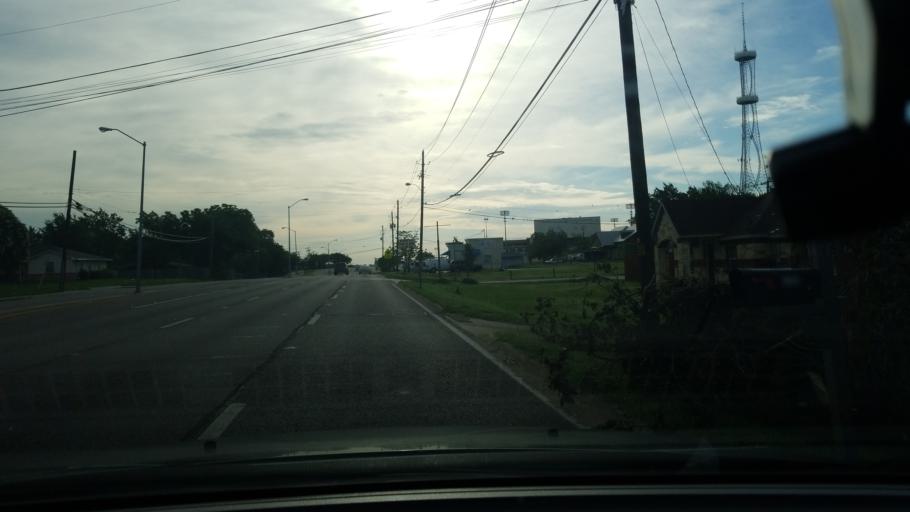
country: US
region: Texas
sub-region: Dallas County
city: Balch Springs
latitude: 32.7636
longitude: -96.6399
